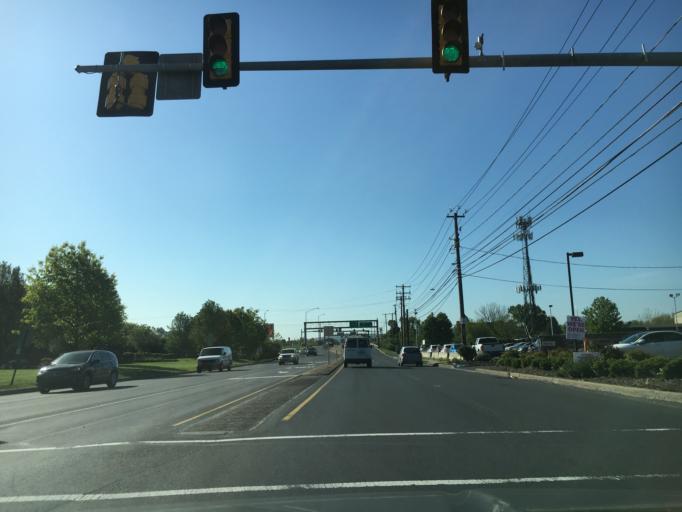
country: US
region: Pennsylvania
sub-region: Northampton County
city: Bethlehem
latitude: 40.6522
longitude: -75.4132
